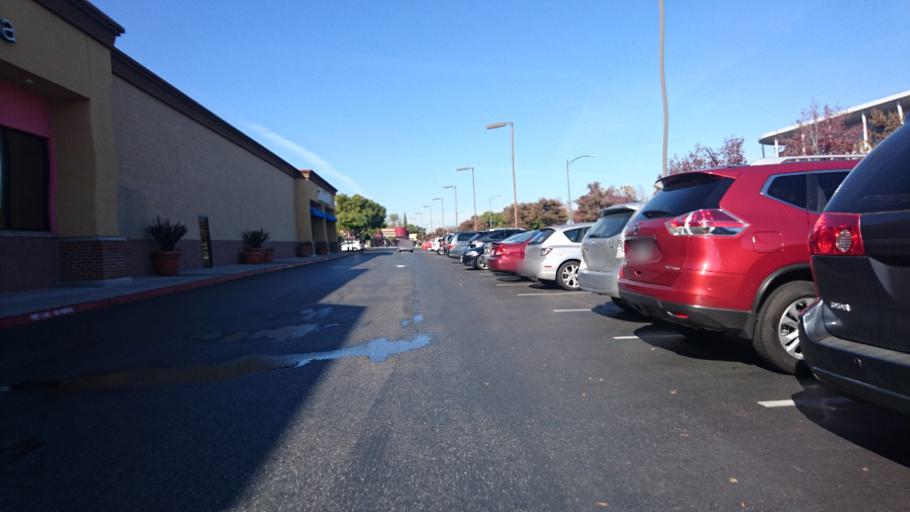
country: US
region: California
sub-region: Santa Clara County
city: Campbell
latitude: 37.2888
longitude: -121.9886
